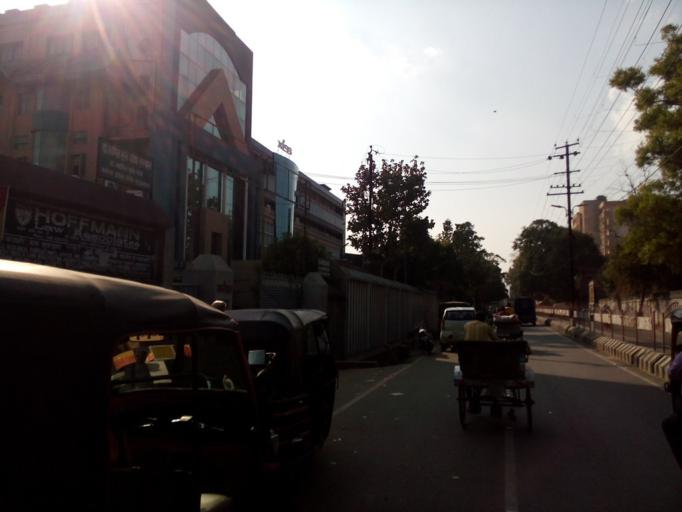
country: IN
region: Jharkhand
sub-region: Ranchi
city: Ranchi
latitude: 23.3683
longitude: 85.3294
